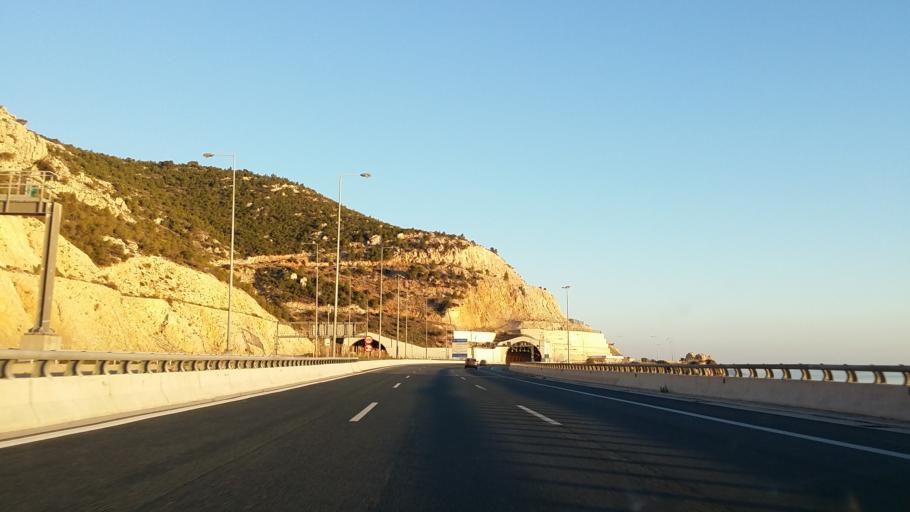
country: GR
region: Attica
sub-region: Nomarchia Dytikis Attikis
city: Megara
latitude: 37.9760
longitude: 23.2886
